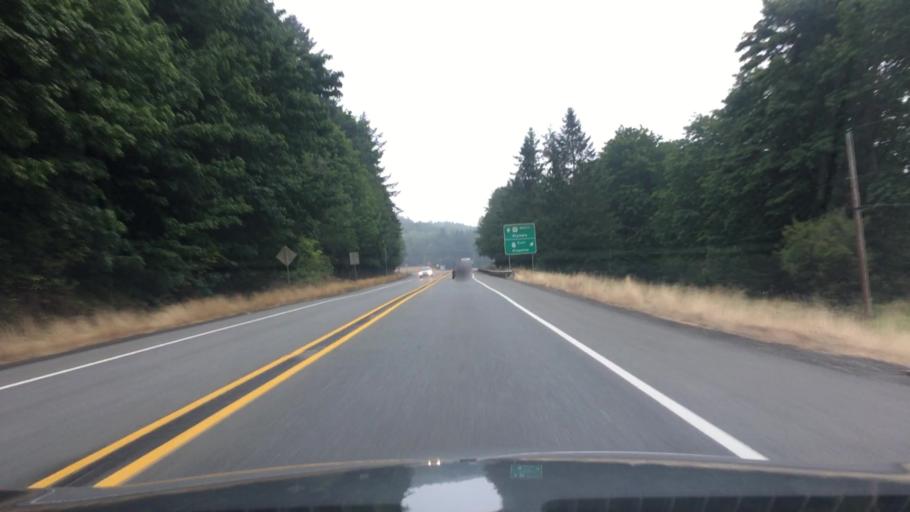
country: US
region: Washington
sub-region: Jefferson County
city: Port Hadlock-Irondale
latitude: 47.9601
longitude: -122.8827
